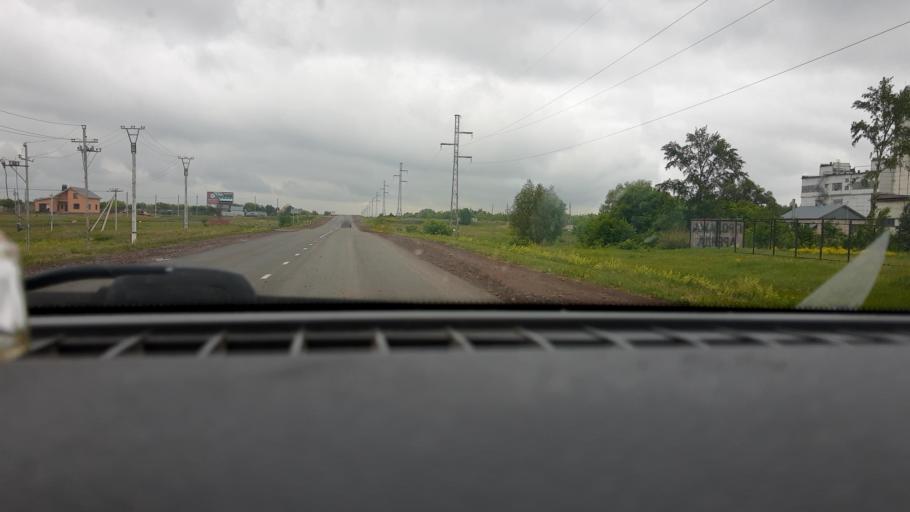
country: RU
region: Bashkortostan
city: Priyutovo
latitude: 53.9069
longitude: 53.9431
